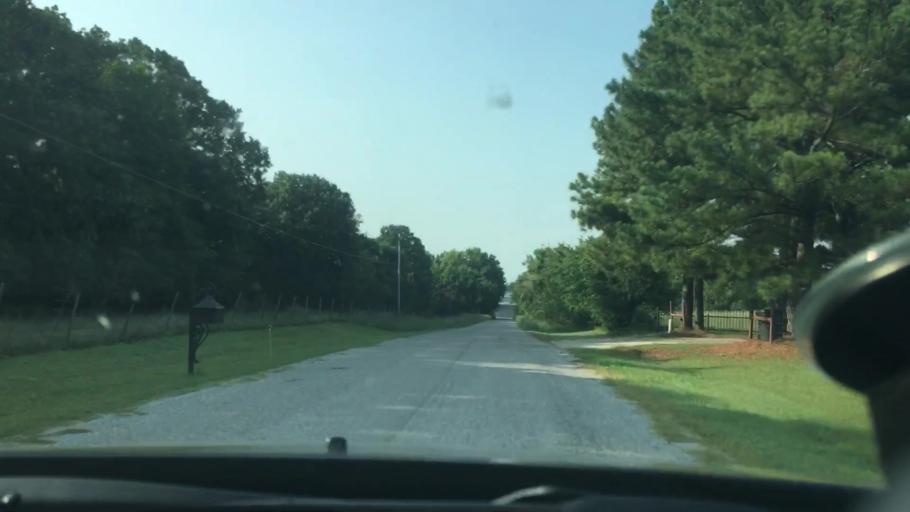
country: US
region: Oklahoma
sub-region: Pontotoc County
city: Ada
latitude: 34.7934
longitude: -96.7397
